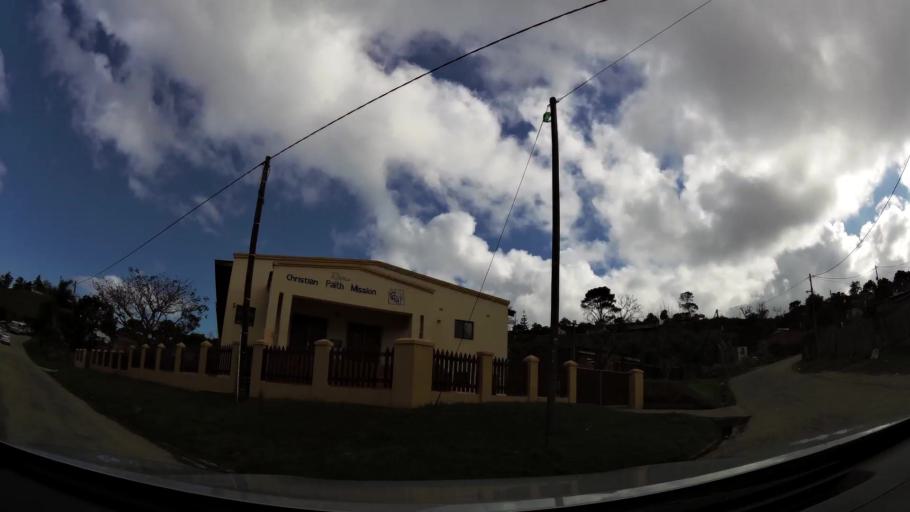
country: ZA
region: Western Cape
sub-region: Eden District Municipality
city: Knysna
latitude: -34.0489
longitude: 23.0918
